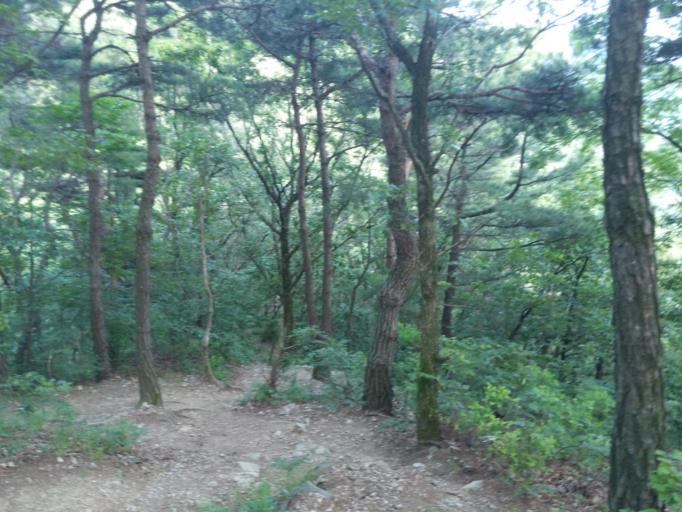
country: KR
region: Daegu
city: Hwawon
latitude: 35.7873
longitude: 128.5421
